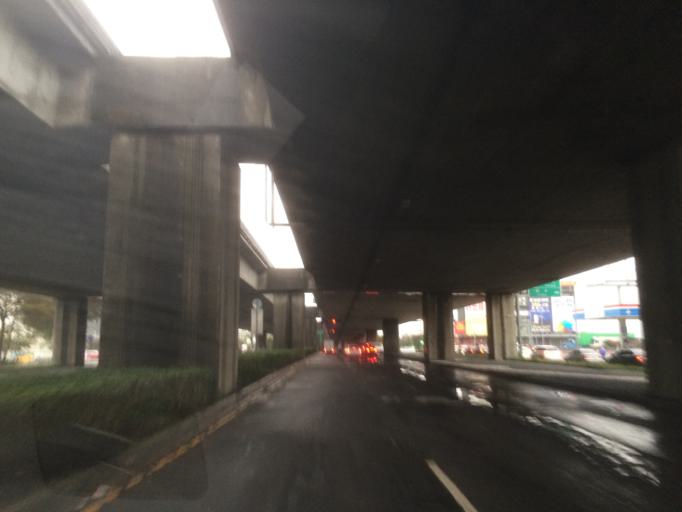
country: TW
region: Taiwan
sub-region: Taichung City
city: Taichung
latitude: 24.1465
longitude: 120.6232
